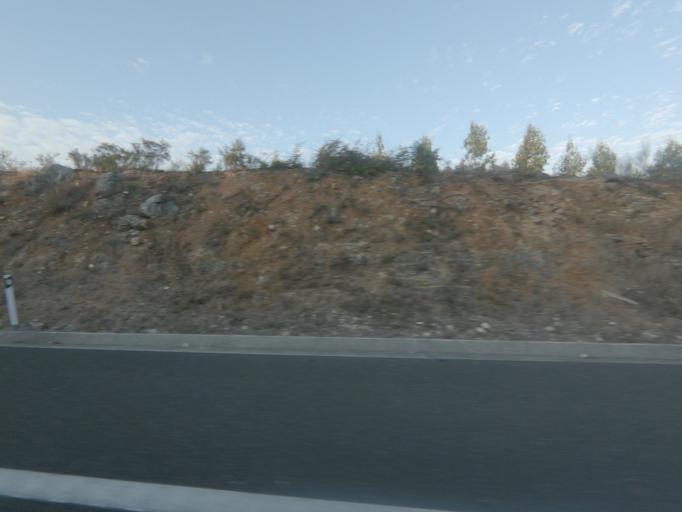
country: PT
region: Leiria
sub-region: Leiria
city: Santa Catarina da Serra
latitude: 39.6853
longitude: -8.6868
